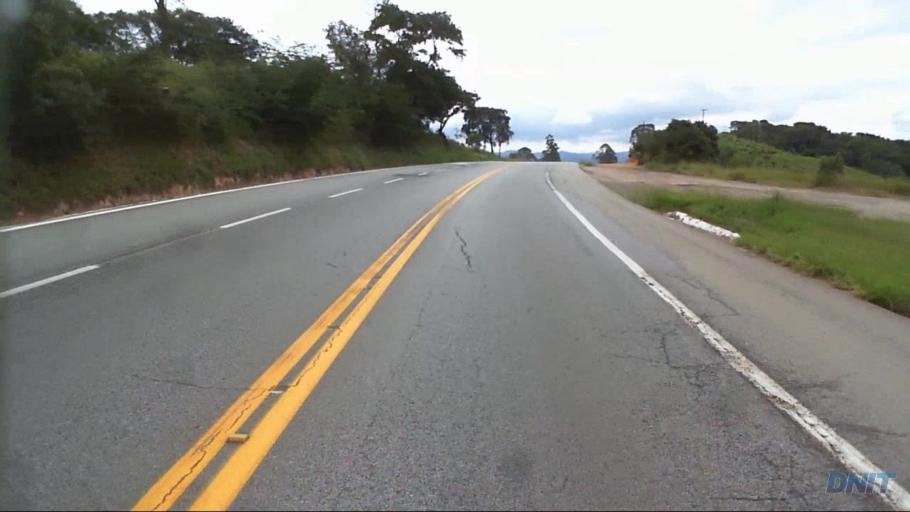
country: BR
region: Minas Gerais
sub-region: Caete
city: Caete
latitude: -19.7351
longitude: -43.5587
